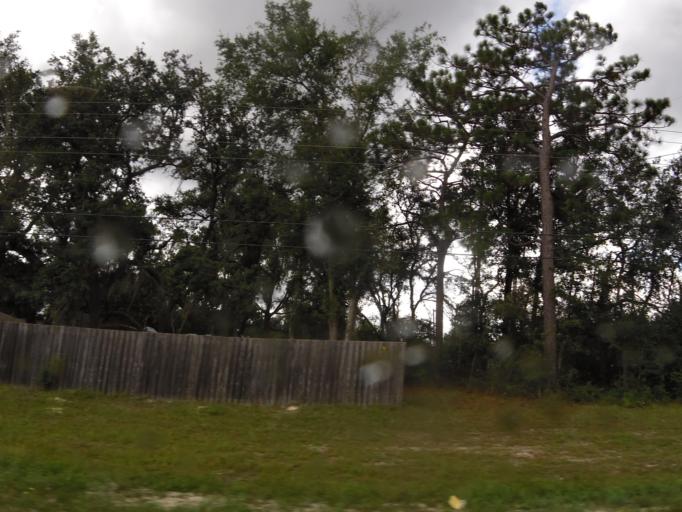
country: US
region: Florida
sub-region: Clay County
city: Asbury Lake
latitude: 30.0391
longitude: -81.8349
